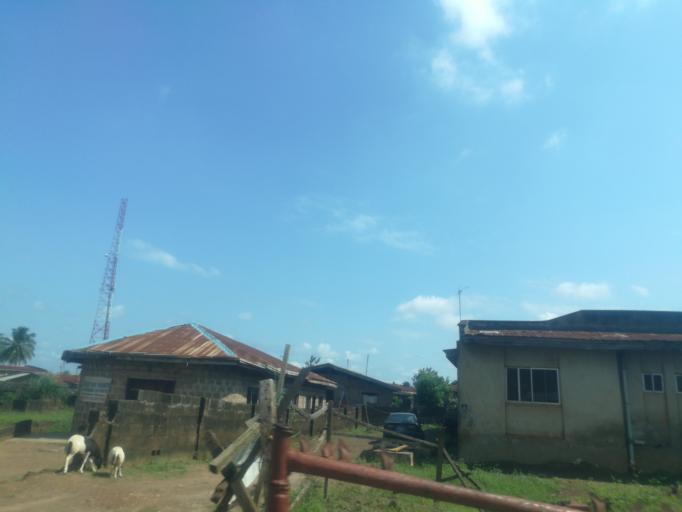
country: NG
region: Oyo
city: Egbeda
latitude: 7.4196
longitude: 3.9857
